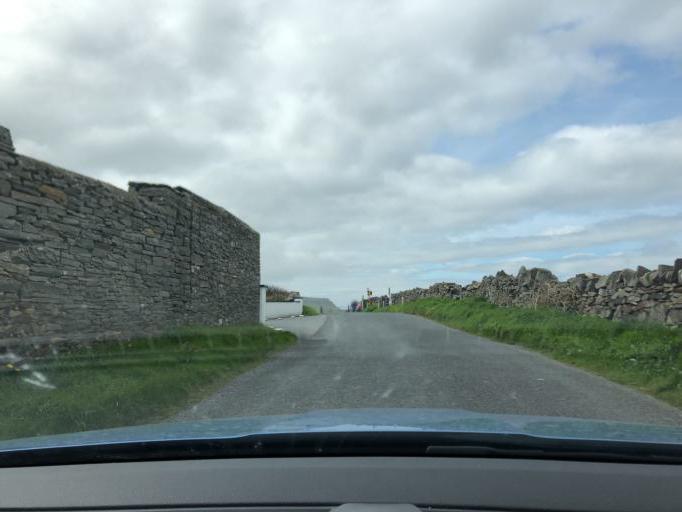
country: IE
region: Connaught
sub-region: County Galway
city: Bearna
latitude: 53.0104
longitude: -9.3877
